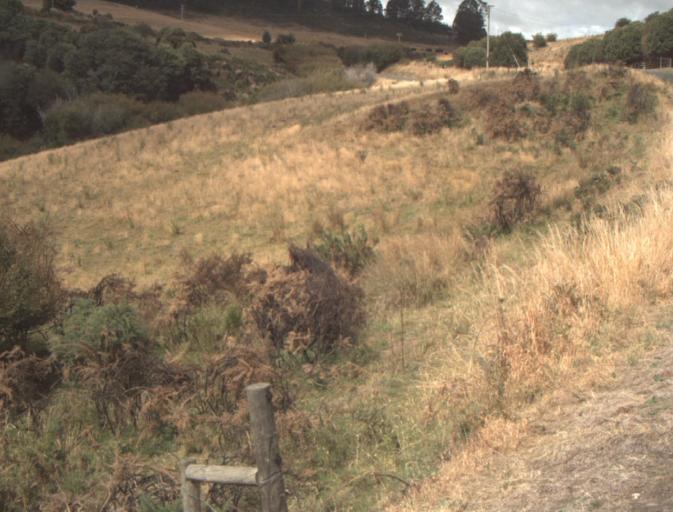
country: AU
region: Tasmania
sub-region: Northern Midlands
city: Evandale
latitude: -41.5137
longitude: 147.4718
